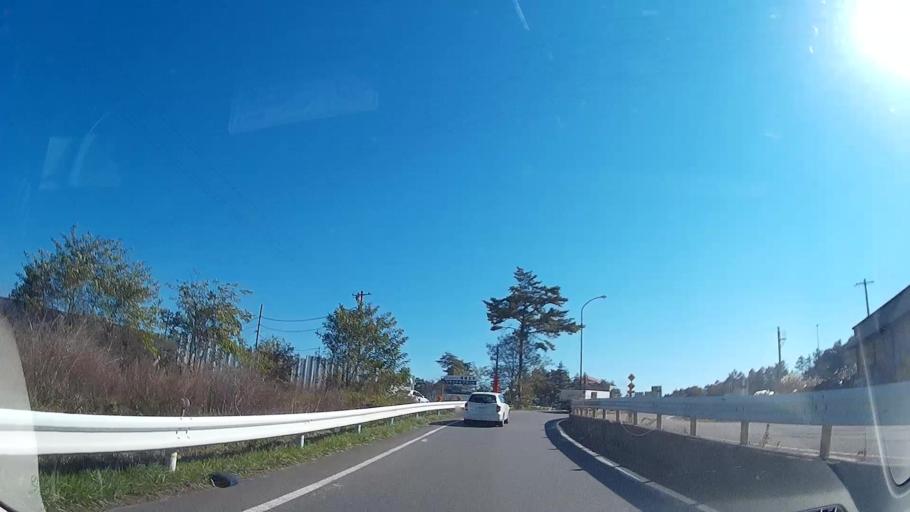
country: JP
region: Nagano
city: Okaya
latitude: 36.0753
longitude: 138.0332
